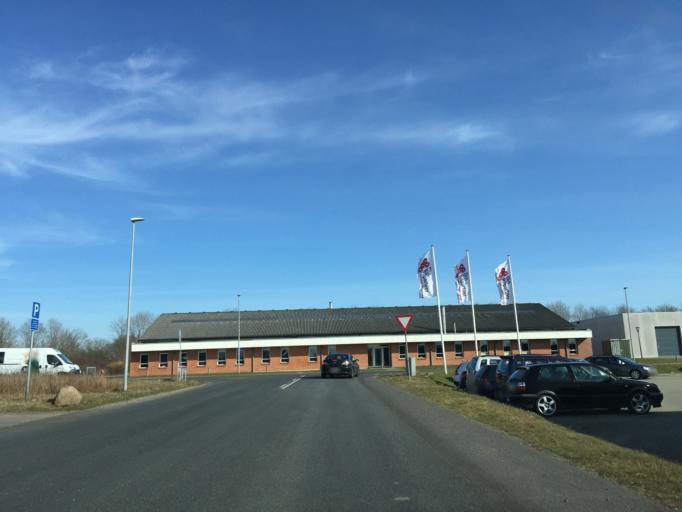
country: DK
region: Central Jutland
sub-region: Silkeborg Kommune
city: Silkeborg
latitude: 56.2021
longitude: 9.5784
